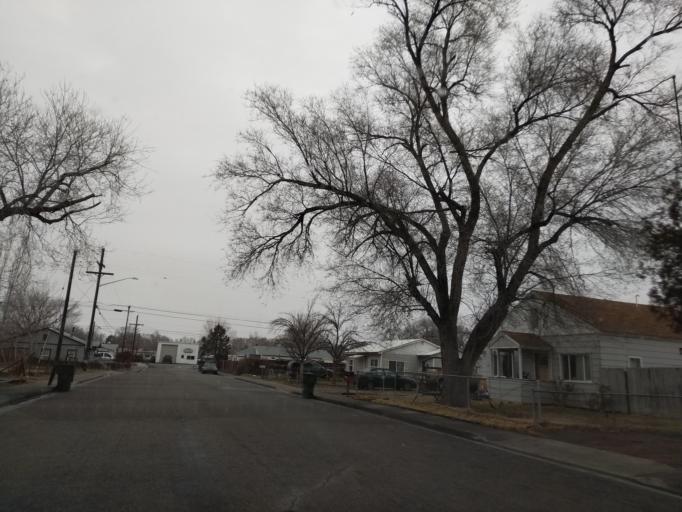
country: US
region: Colorado
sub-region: Mesa County
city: Fruitvale
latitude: 39.0755
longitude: -108.5231
